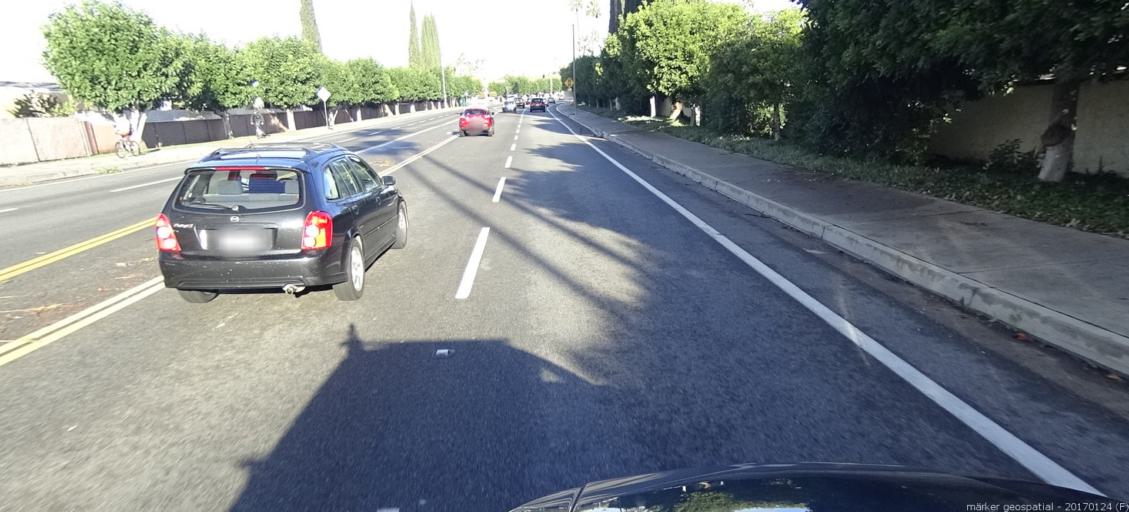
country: US
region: California
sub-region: Orange County
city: Laguna Hills
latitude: 33.6180
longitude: -117.6934
